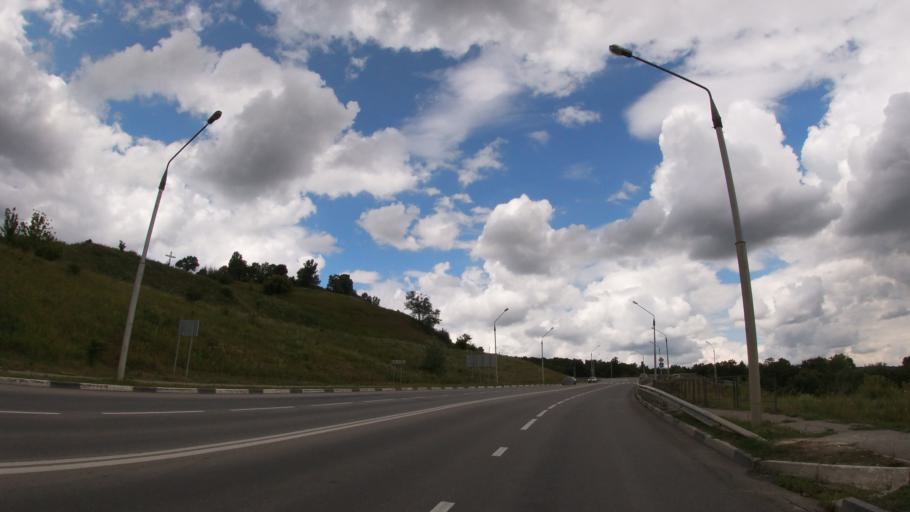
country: RU
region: Belgorod
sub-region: Belgorodskiy Rayon
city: Belgorod
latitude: 50.6182
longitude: 36.6164
